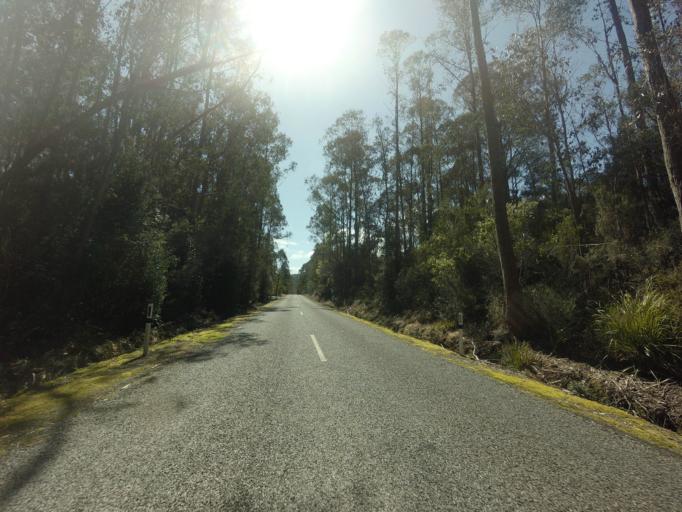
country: AU
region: Tasmania
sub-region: Derwent Valley
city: New Norfolk
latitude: -42.7425
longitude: 146.4175
